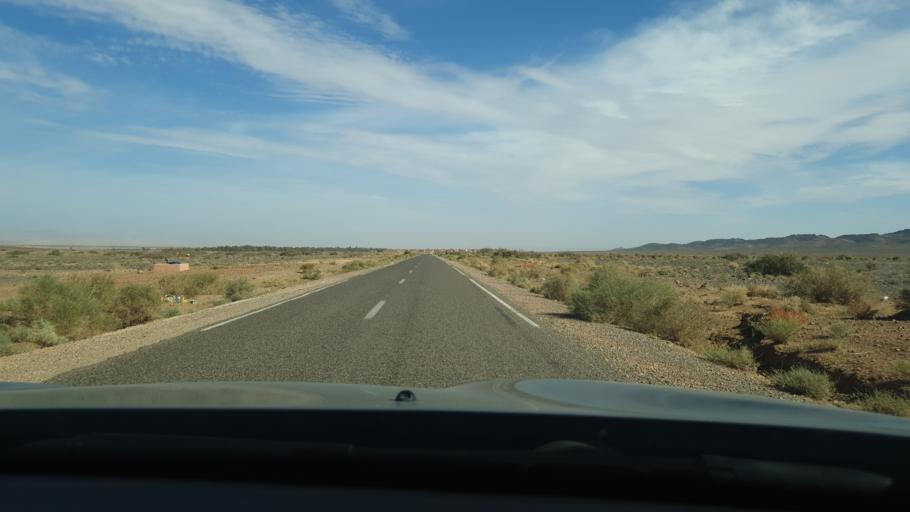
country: MA
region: Meknes-Tafilalet
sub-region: Errachidia
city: Goulmima
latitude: 31.5131
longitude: -4.9862
